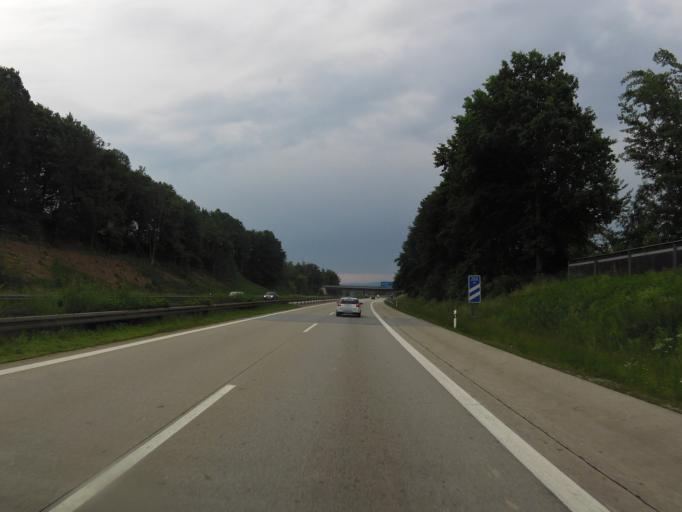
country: DE
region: Bavaria
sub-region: Lower Bavaria
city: Iggensbach
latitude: 48.7256
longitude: 13.1387
